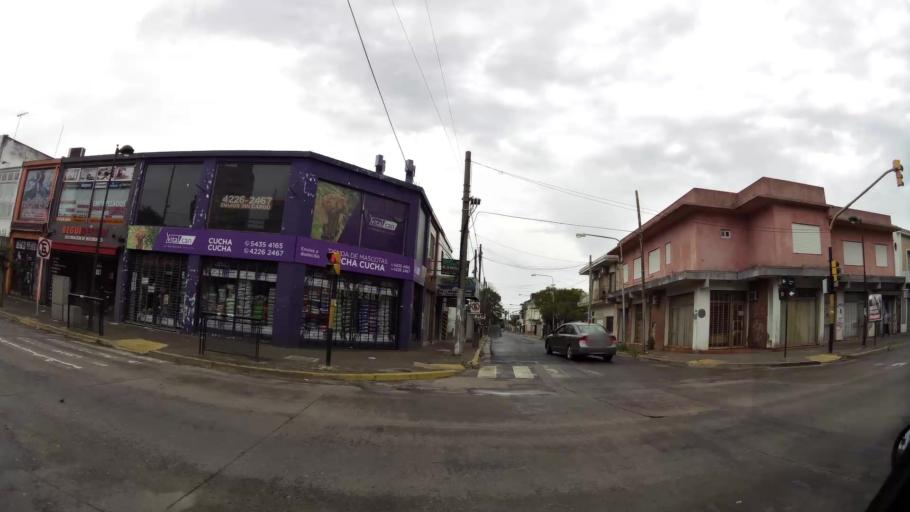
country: AR
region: Buenos Aires
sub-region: Partido de Quilmes
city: Quilmes
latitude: -34.7585
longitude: -58.2059
